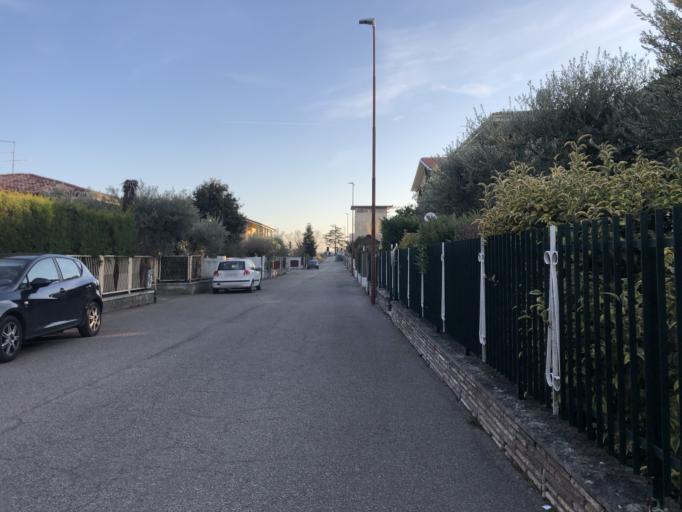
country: IT
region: Veneto
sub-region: Provincia di Verona
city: Pastrengo
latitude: 45.4764
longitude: 10.8230
